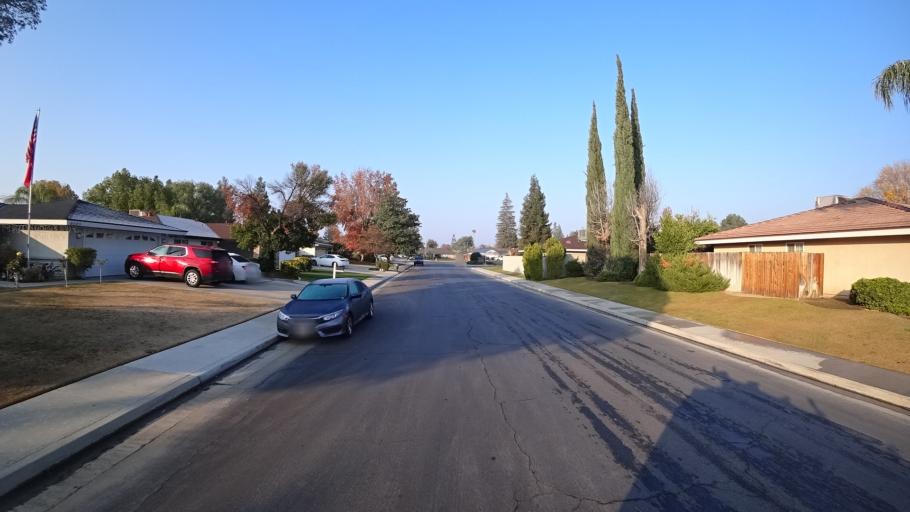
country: US
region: California
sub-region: Kern County
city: Greenacres
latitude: 35.3223
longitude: -119.0764
